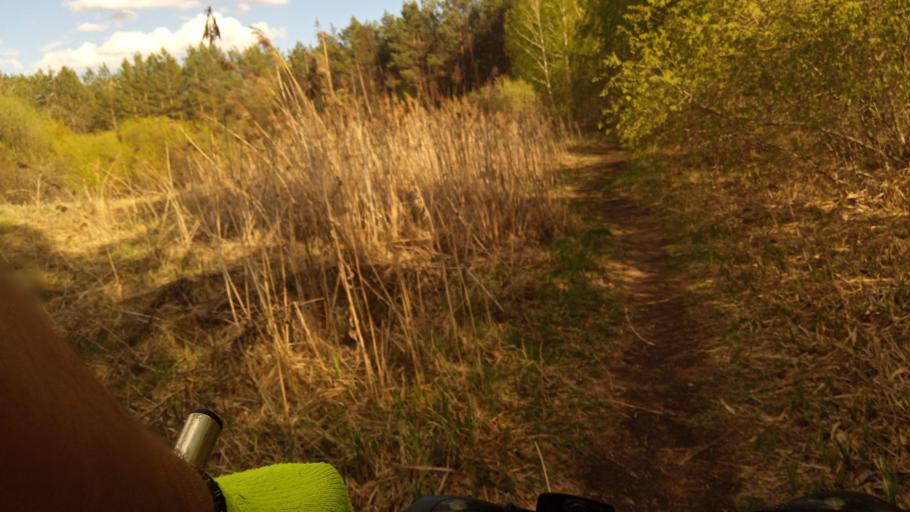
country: RU
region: Chelyabinsk
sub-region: Gorod Chelyabinsk
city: Chelyabinsk
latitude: 55.1580
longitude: 61.3203
